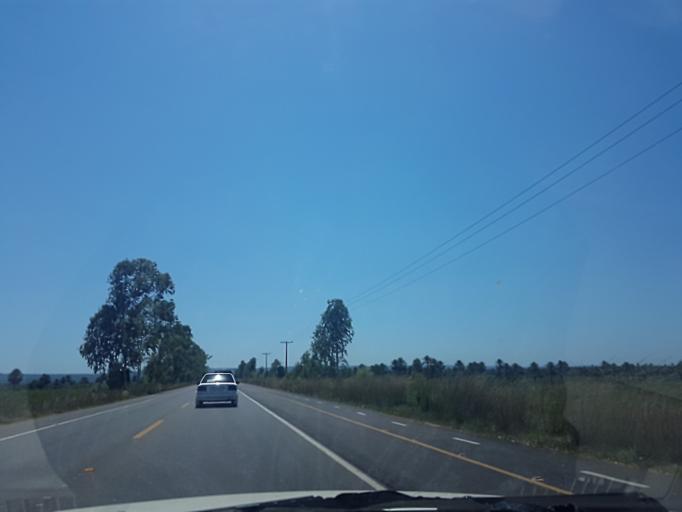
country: PY
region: Cordillera
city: Emboscada
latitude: -25.2094
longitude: -57.4092
